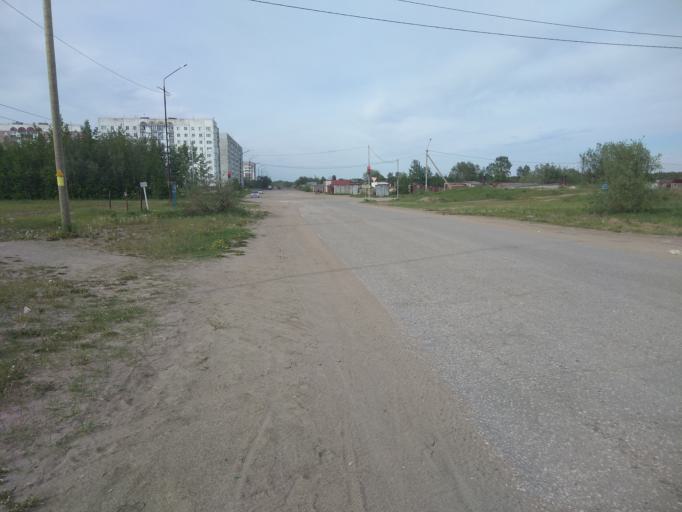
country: RU
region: Komi Republic
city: Pechora
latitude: 65.1446
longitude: 57.2366
